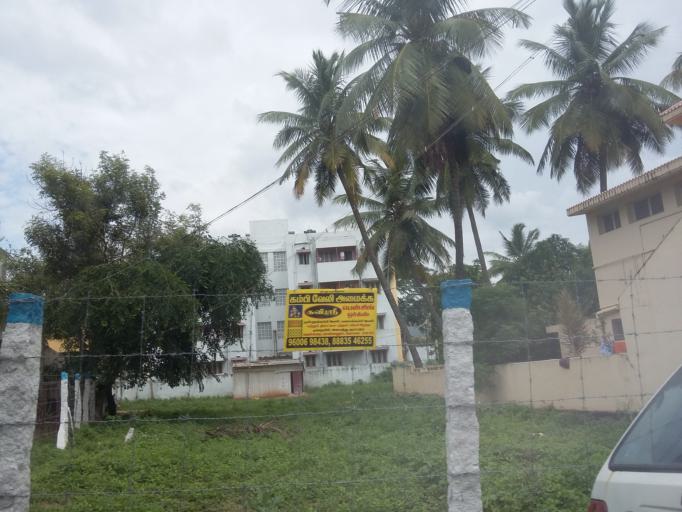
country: IN
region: Tamil Nadu
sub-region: Coimbatore
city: Perur
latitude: 11.0288
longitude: 76.8985
